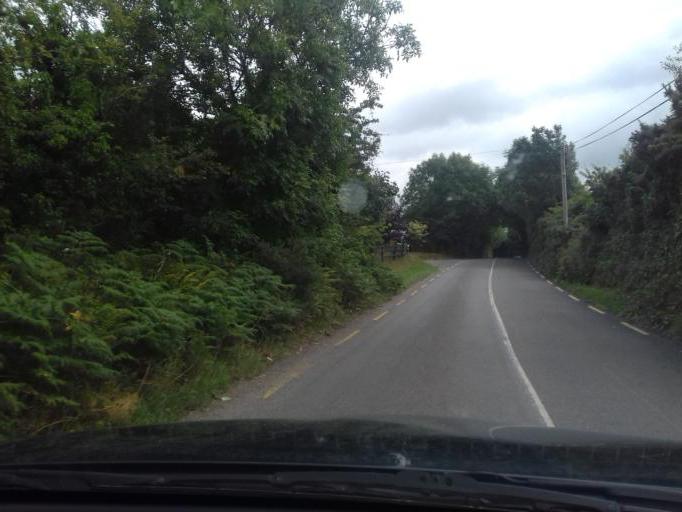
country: IE
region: Leinster
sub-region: Loch Garman
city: Ballinroad
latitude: 52.4743
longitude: -6.4031
